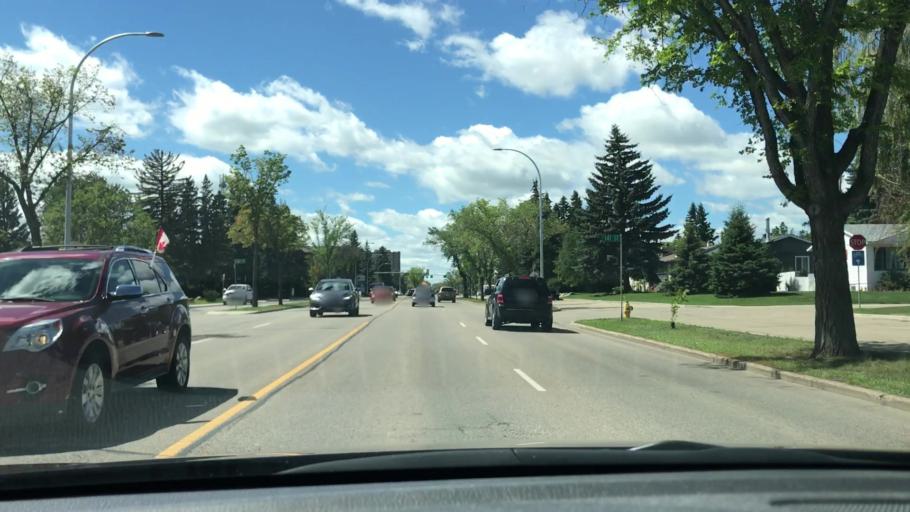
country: CA
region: Alberta
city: Edmonton
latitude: 53.5194
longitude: -113.5743
